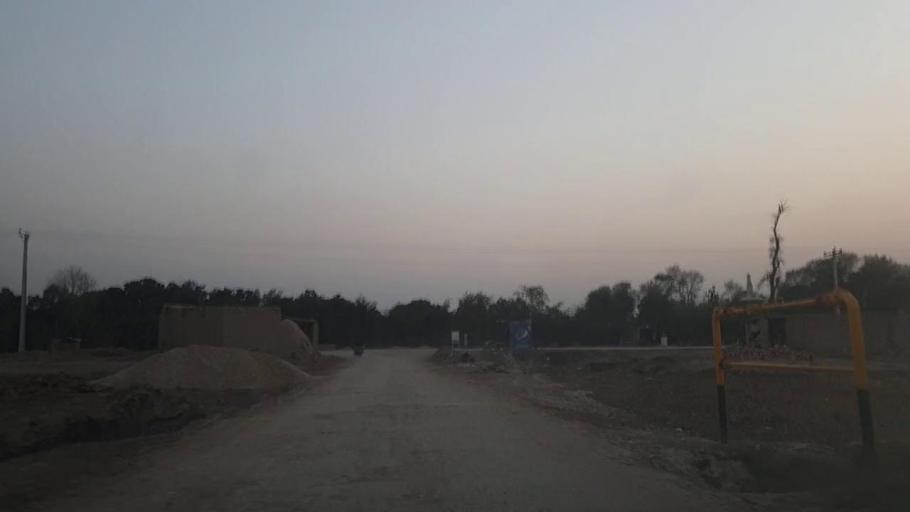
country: PK
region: Sindh
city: Naushahro Firoz
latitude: 26.8497
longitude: 68.0480
